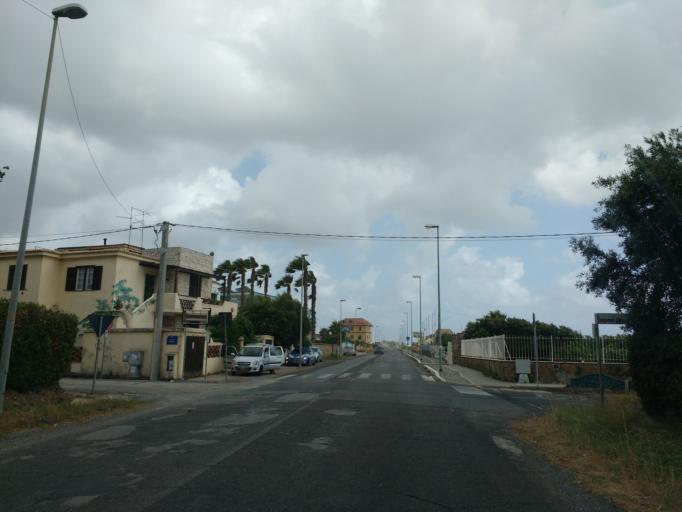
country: IT
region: Latium
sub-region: Citta metropolitana di Roma Capitale
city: Anzio
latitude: 41.4751
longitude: 12.6033
